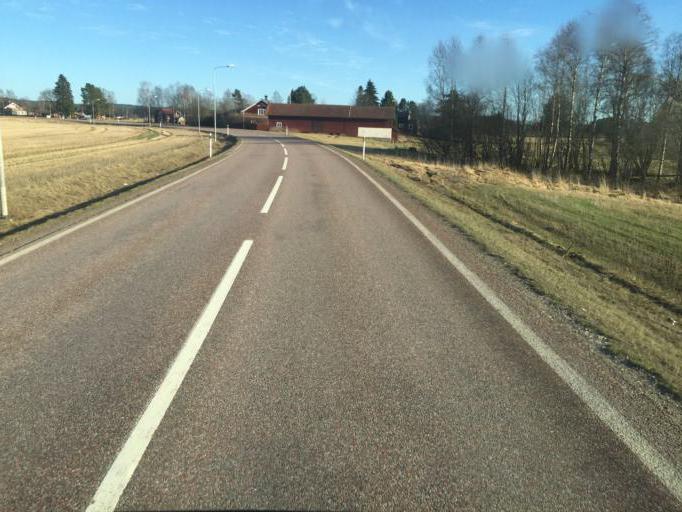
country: SE
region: Dalarna
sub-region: Vansbro Kommun
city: Jarna
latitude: 60.4507
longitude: 14.5066
